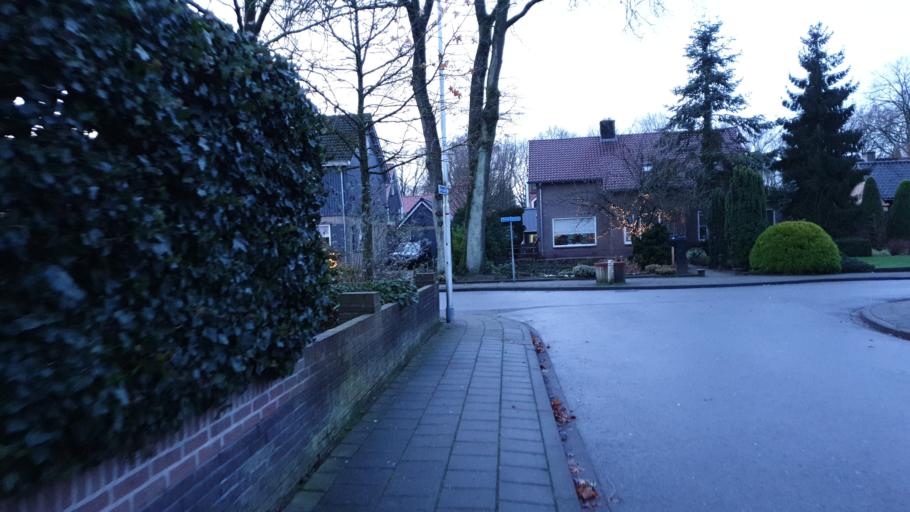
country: NL
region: Gelderland
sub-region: Gemeente Ede
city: Otterlo
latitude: 52.0998
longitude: 5.7740
